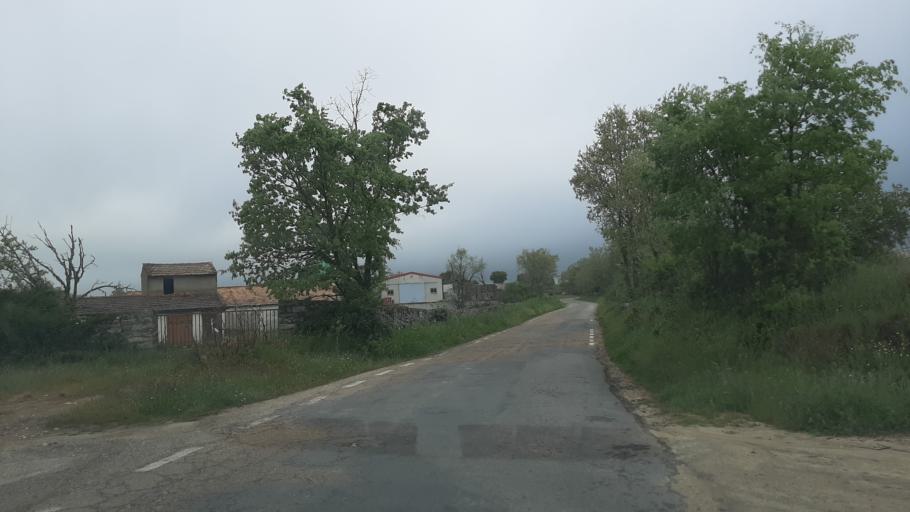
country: ES
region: Castille and Leon
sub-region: Provincia de Salamanca
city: Endrinal
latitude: 40.5538
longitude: -5.8066
